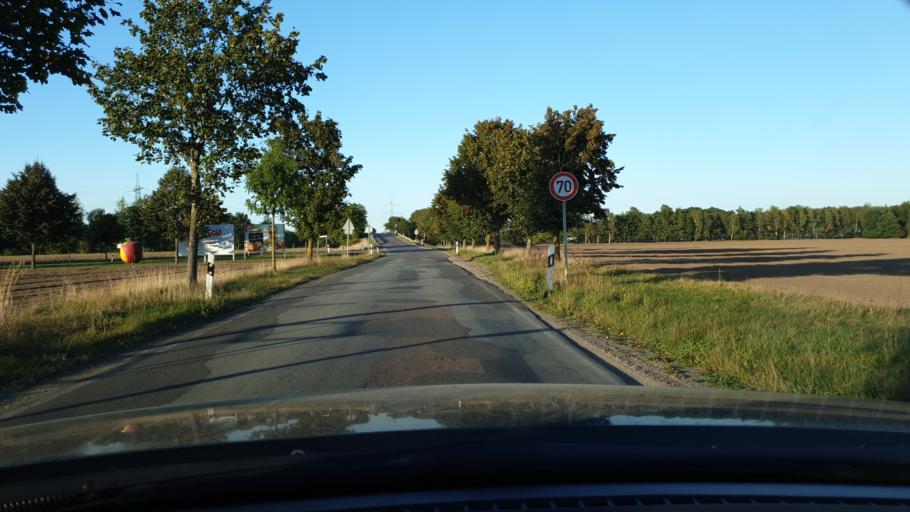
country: DE
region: Mecklenburg-Vorpommern
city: Wittenburg
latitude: 53.5044
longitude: 11.0032
